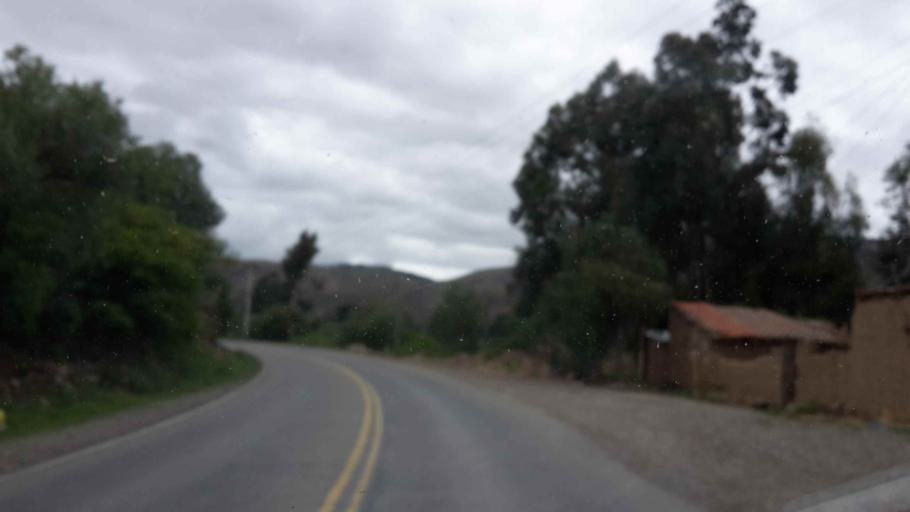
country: BO
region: Cochabamba
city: Punata
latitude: -17.5137
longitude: -65.8131
